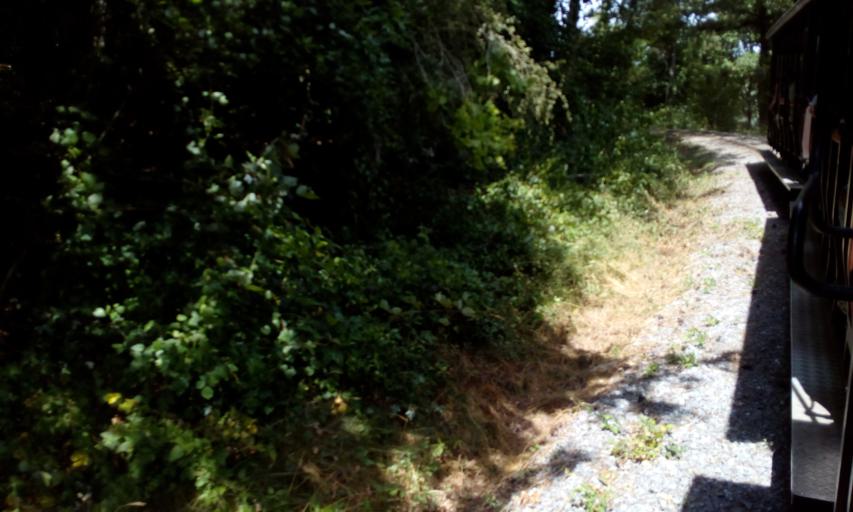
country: BE
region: Wallonia
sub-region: Province de Namur
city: Rochefort
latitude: 50.1245
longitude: 5.2064
